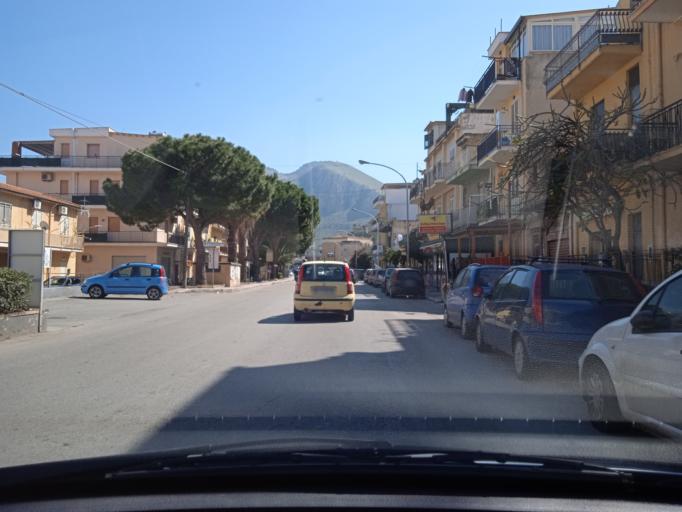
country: IT
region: Sicily
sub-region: Palermo
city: Villabate
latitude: 38.0842
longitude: 13.4337
